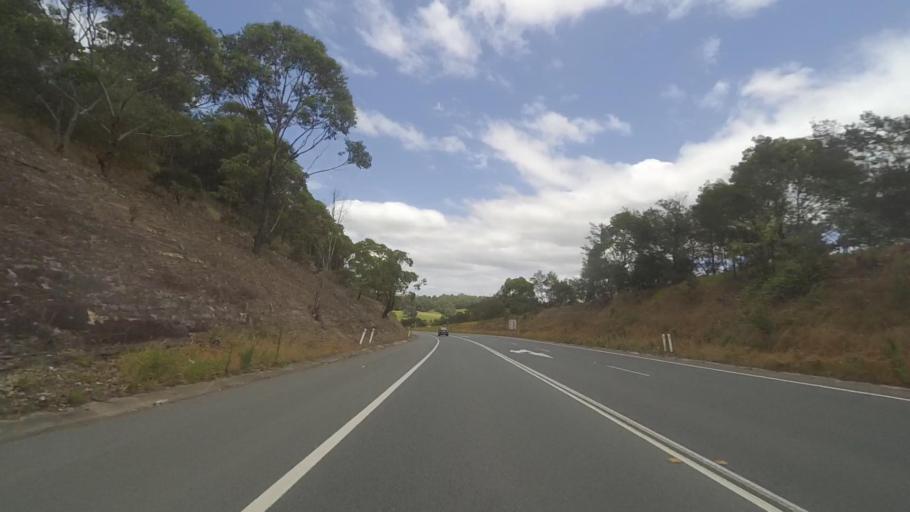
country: AU
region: New South Wales
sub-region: Shoalhaven Shire
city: Milton
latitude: -35.2638
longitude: 150.4261
